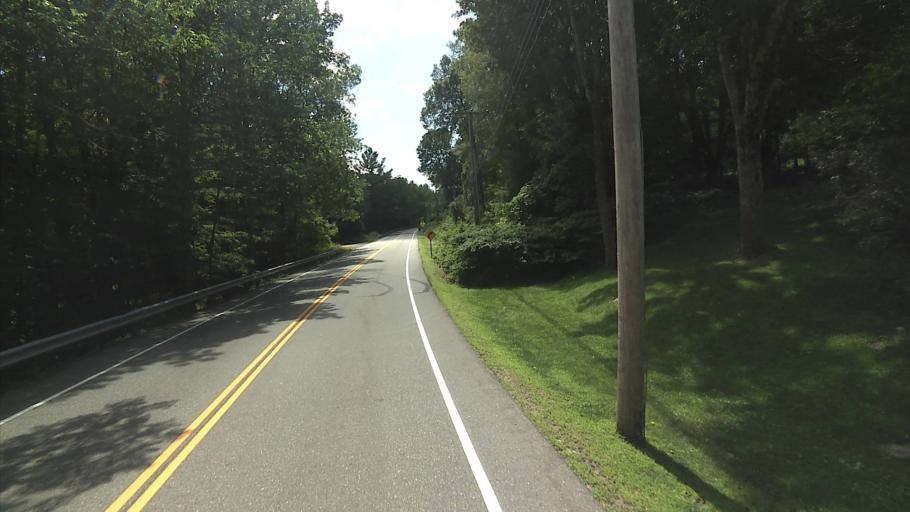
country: US
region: Connecticut
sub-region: Windham County
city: South Woodstock
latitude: 41.9534
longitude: -72.0760
